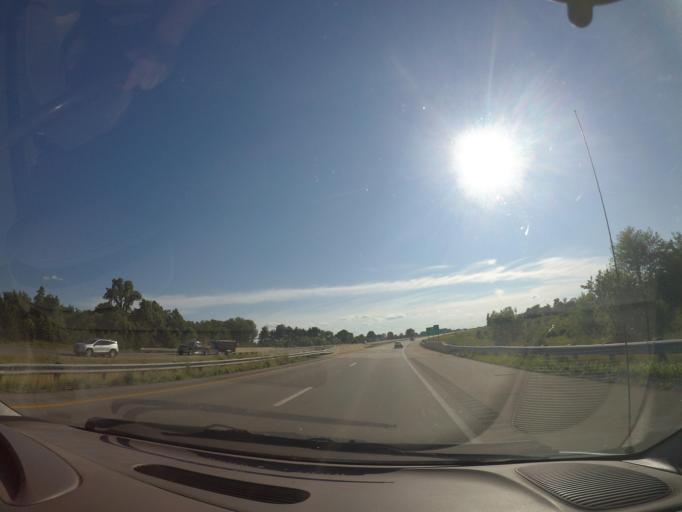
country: US
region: Ohio
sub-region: Henry County
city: Liberty Center
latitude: 41.4296
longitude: -83.9907
